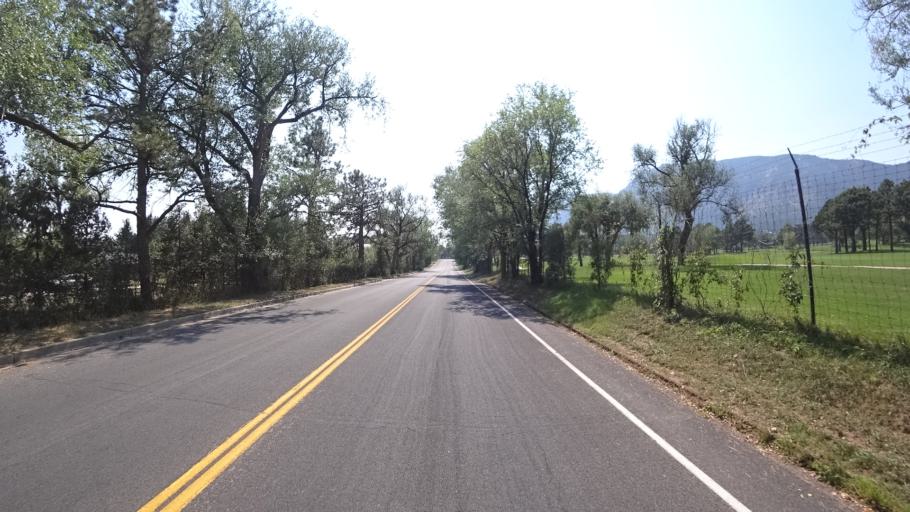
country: US
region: Colorado
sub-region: El Paso County
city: Colorado Springs
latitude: 38.7848
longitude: -104.8455
